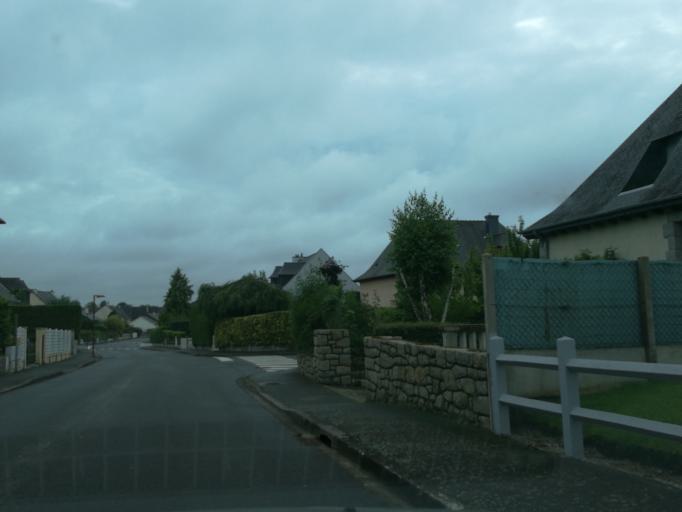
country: FR
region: Brittany
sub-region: Departement d'Ille-et-Vilaine
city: Bedee
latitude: 48.1796
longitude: -1.9401
